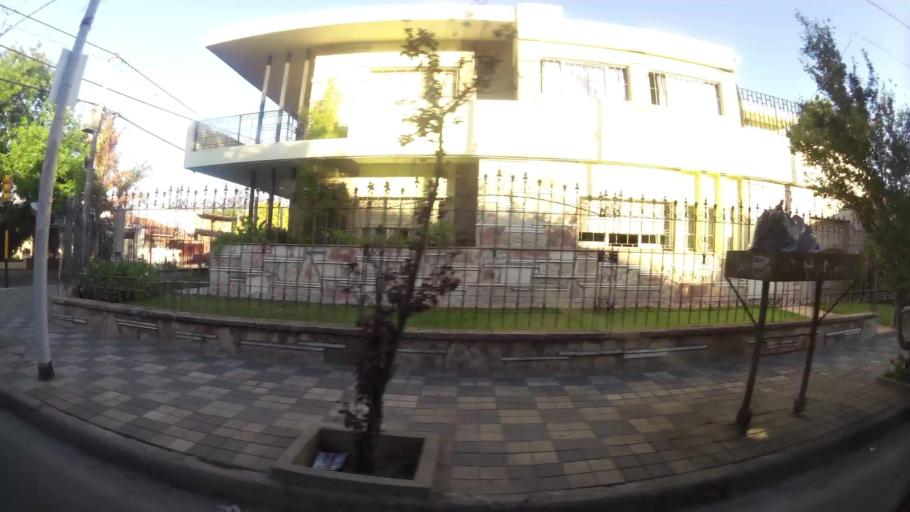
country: AR
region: Cordoba
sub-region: Departamento de Capital
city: Cordoba
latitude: -31.3843
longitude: -64.2168
